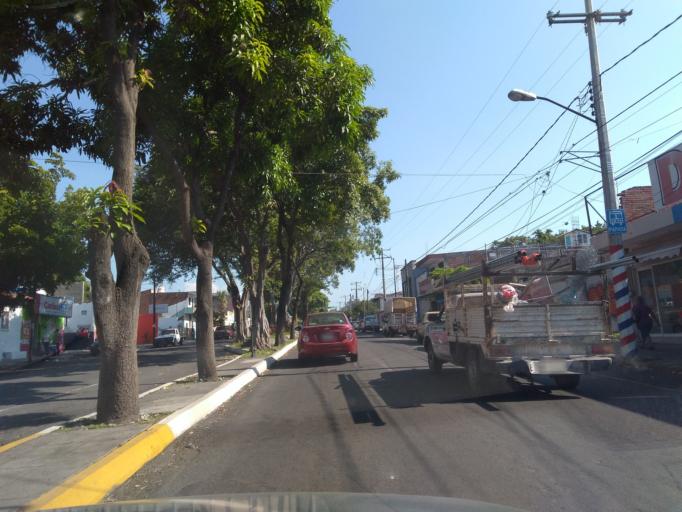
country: MX
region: Colima
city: Colima
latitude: 19.2501
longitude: -103.7321
